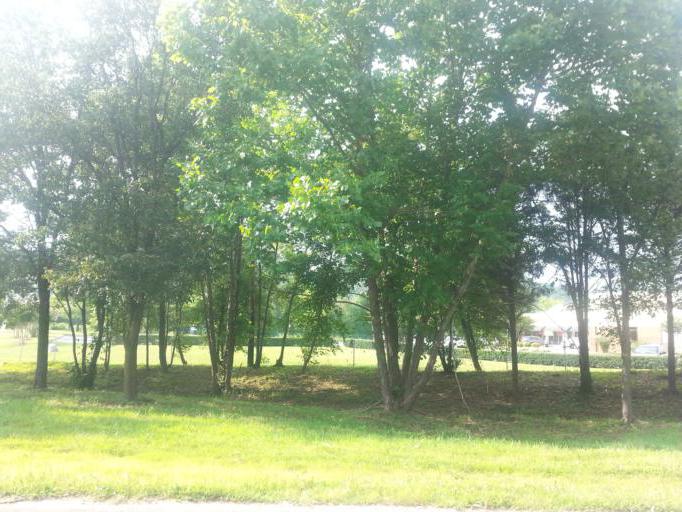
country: US
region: Tennessee
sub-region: Knox County
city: Knoxville
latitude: 36.0335
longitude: -83.8866
